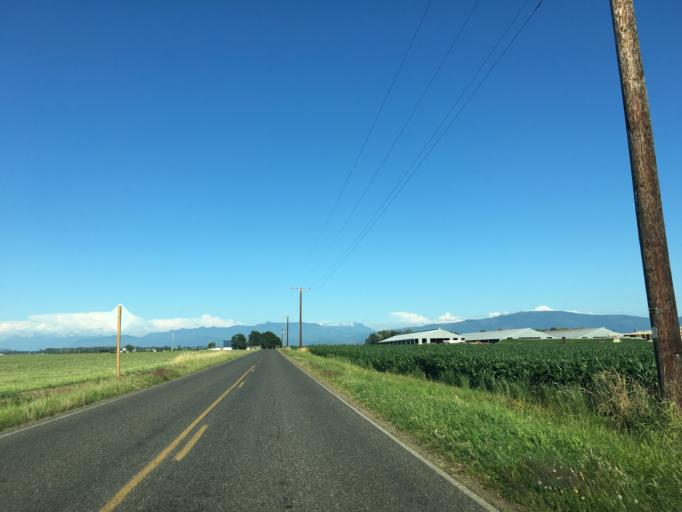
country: US
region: Washington
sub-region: Whatcom County
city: Lynden
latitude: 48.9865
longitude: -122.4613
